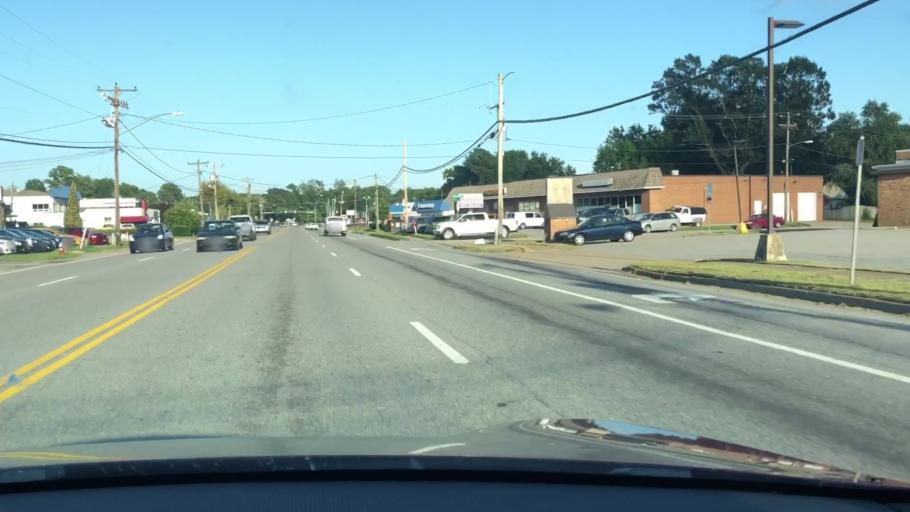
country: US
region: Virginia
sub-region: City of Virginia Beach
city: Virginia Beach
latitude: 36.8430
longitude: -76.0257
